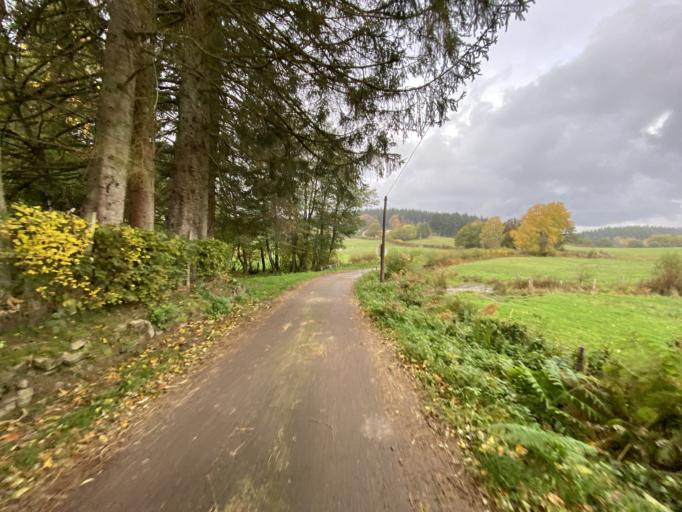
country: FR
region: Bourgogne
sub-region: Departement de la Cote-d'Or
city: Saulieu
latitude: 47.2968
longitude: 4.1199
